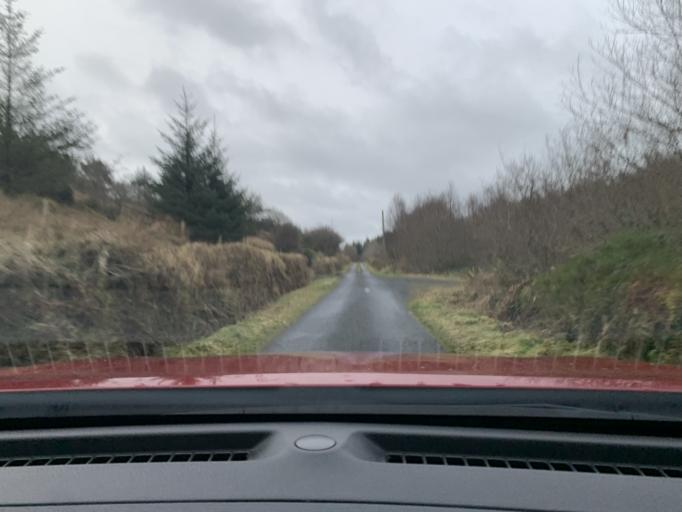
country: IE
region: Connaught
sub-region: Roscommon
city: Boyle
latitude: 54.0052
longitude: -8.3907
